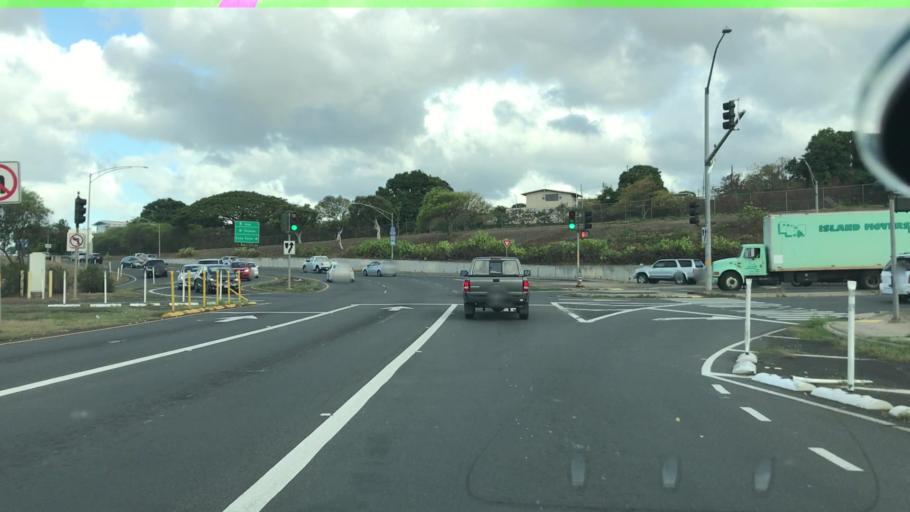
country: US
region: Hawaii
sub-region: Honolulu County
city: Halawa Heights
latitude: 21.3727
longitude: -157.9173
